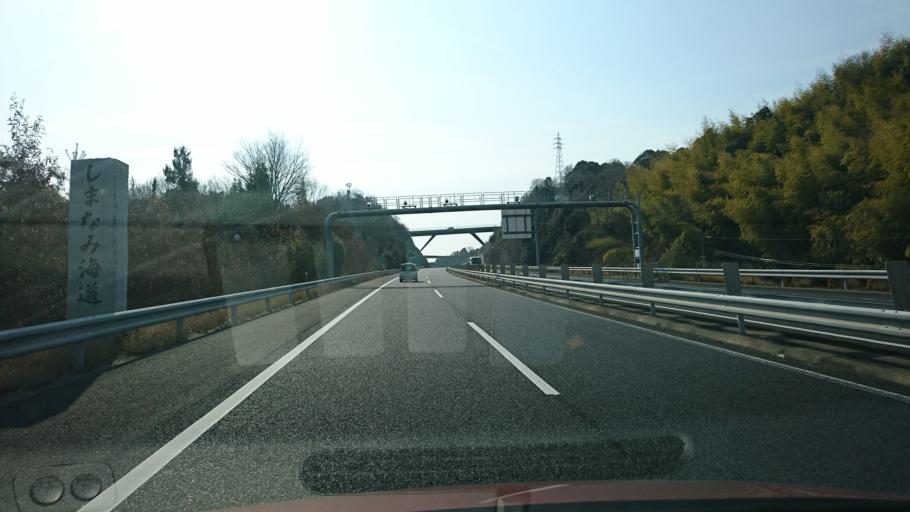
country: JP
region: Hiroshima
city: Onomichi
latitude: 34.4254
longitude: 133.2192
